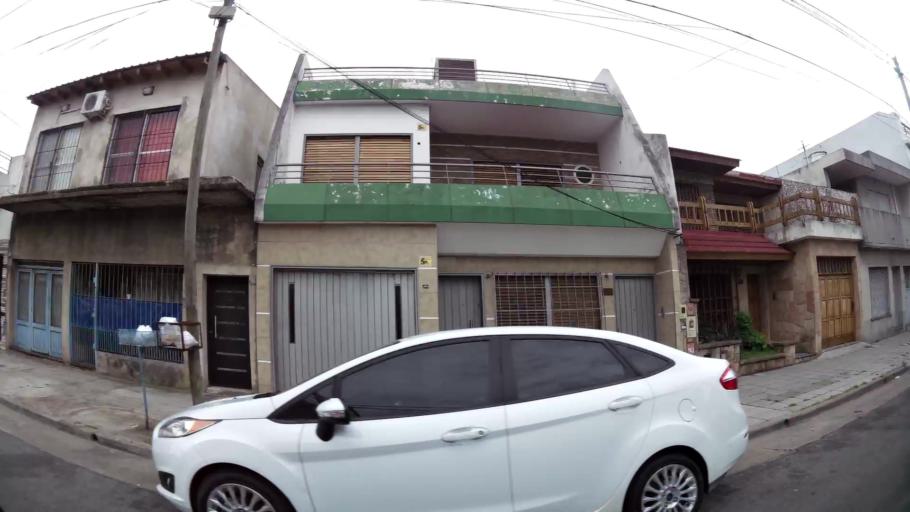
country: AR
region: Buenos Aires
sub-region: Partido de Lanus
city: Lanus
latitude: -34.6769
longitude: -58.3885
